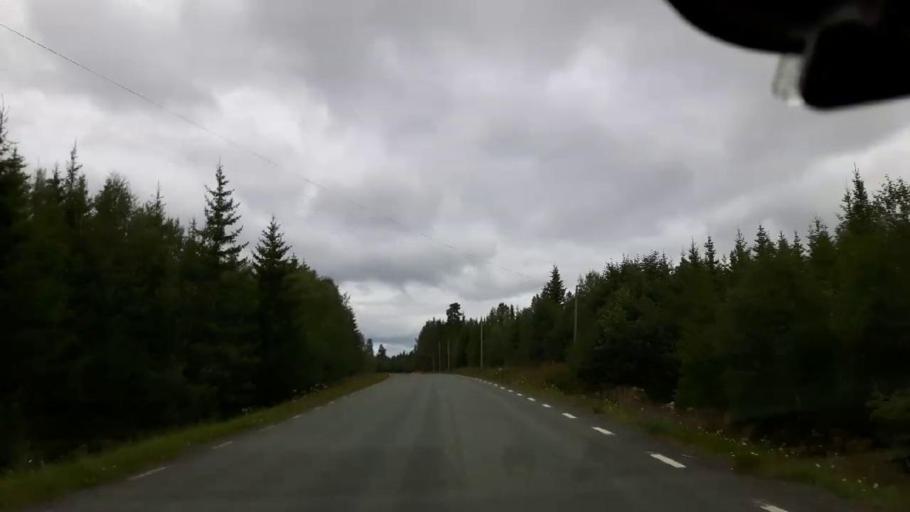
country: SE
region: Jaemtland
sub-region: Krokoms Kommun
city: Valla
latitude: 63.5182
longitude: 13.8754
